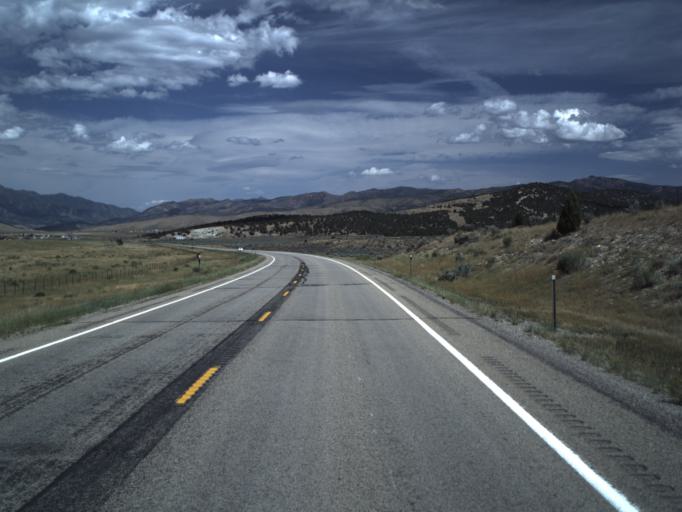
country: US
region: Utah
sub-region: Sanpete County
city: Fairview
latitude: 39.7449
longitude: -111.4774
